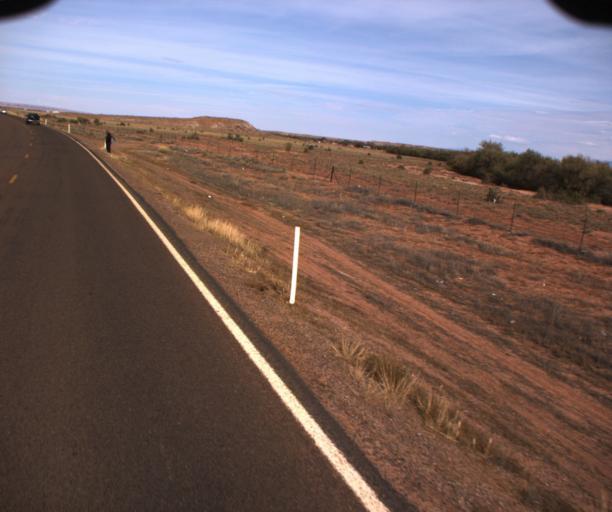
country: US
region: Arizona
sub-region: Apache County
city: Many Farms
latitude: 36.2720
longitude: -109.6001
